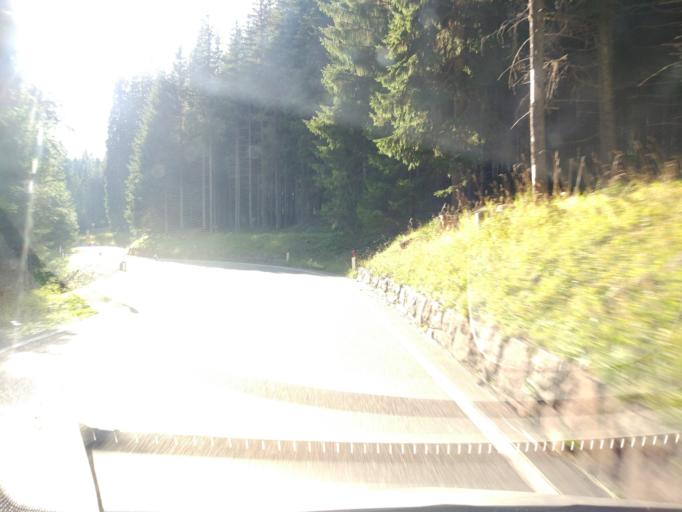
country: IT
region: Veneto
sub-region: Provincia di Belluno
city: Falcade Alto
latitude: 46.3097
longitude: 11.7556
